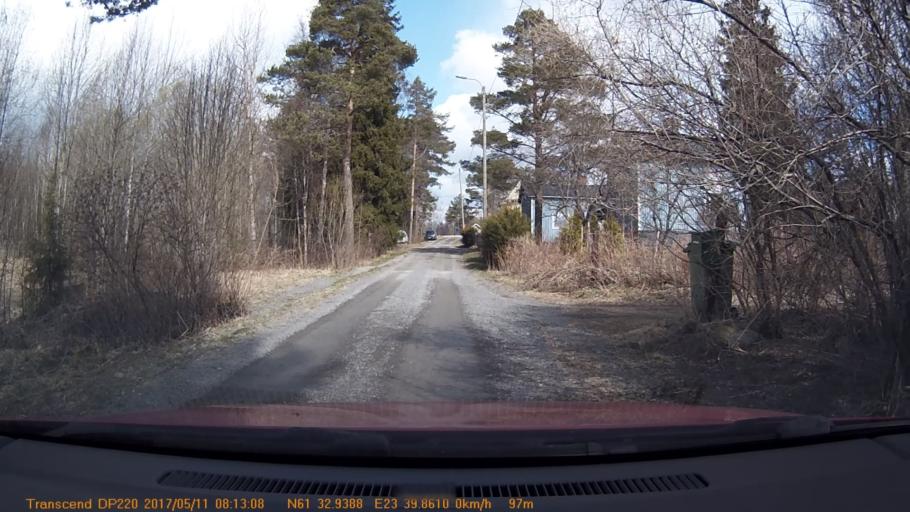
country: FI
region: Pirkanmaa
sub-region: Tampere
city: Yloejaervi
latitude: 61.5490
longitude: 23.6644
